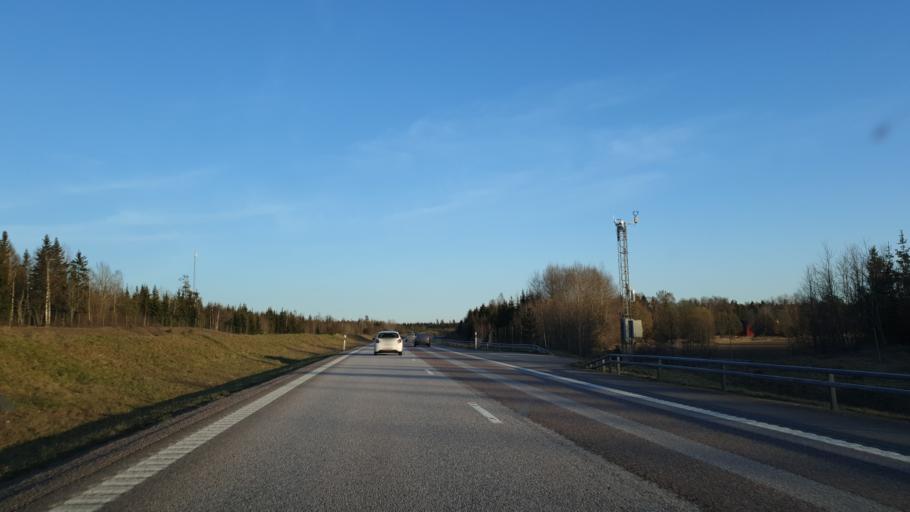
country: SE
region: Uppsala
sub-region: Osthammars Kommun
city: Bjorklinge
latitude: 60.0498
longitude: 17.6224
